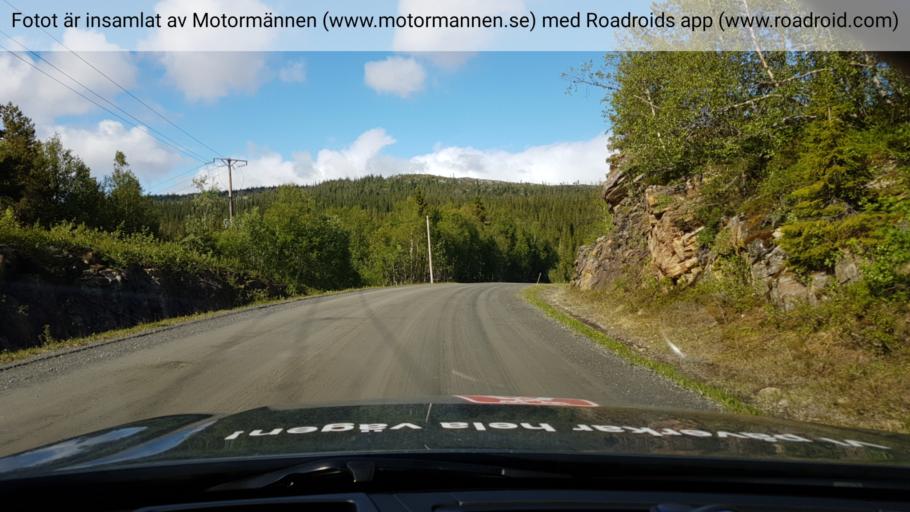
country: SE
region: Jaemtland
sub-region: Are Kommun
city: Are
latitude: 63.6861
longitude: 12.8075
